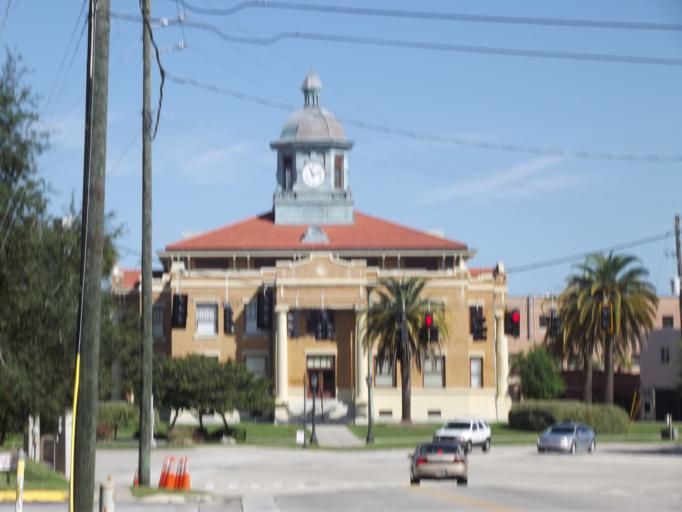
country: US
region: Florida
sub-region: Citrus County
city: Inverness
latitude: 28.8350
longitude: -82.3302
